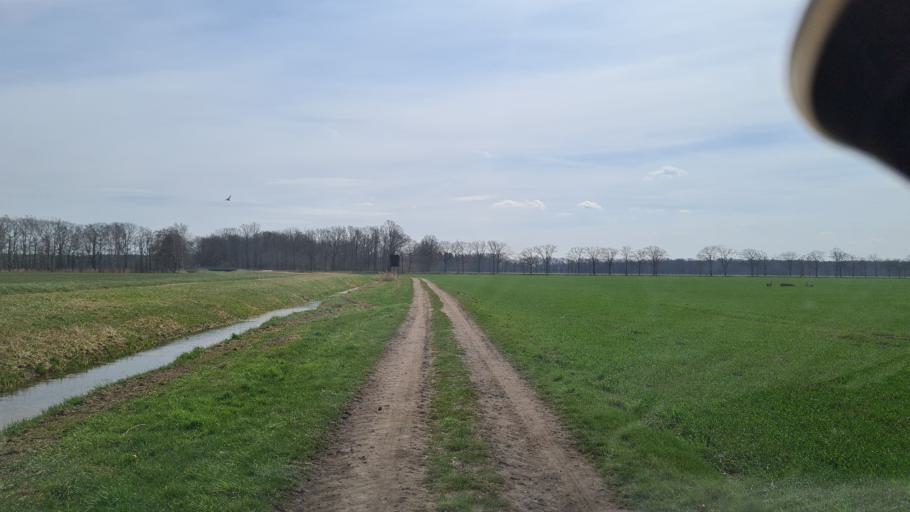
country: DE
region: Brandenburg
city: Bronkow
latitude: 51.6219
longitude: 13.9165
